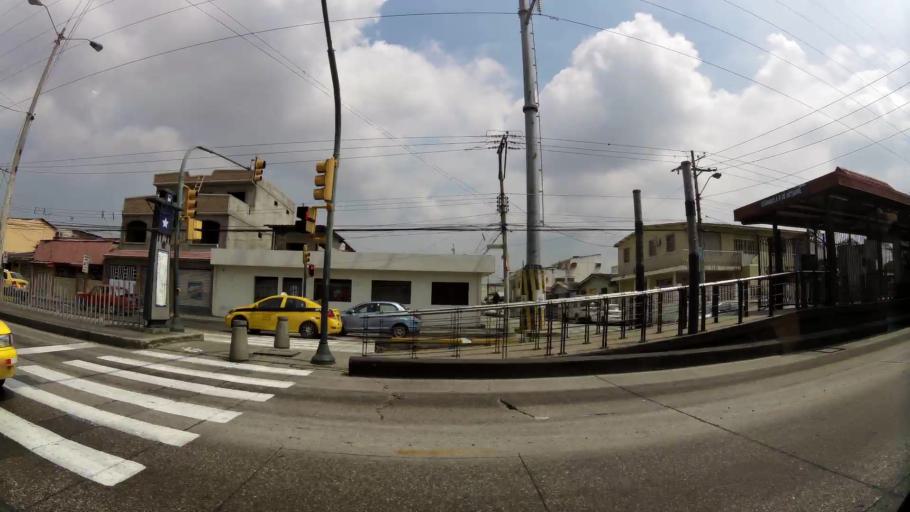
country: EC
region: Guayas
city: Guayaquil
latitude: -2.2328
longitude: -79.8905
